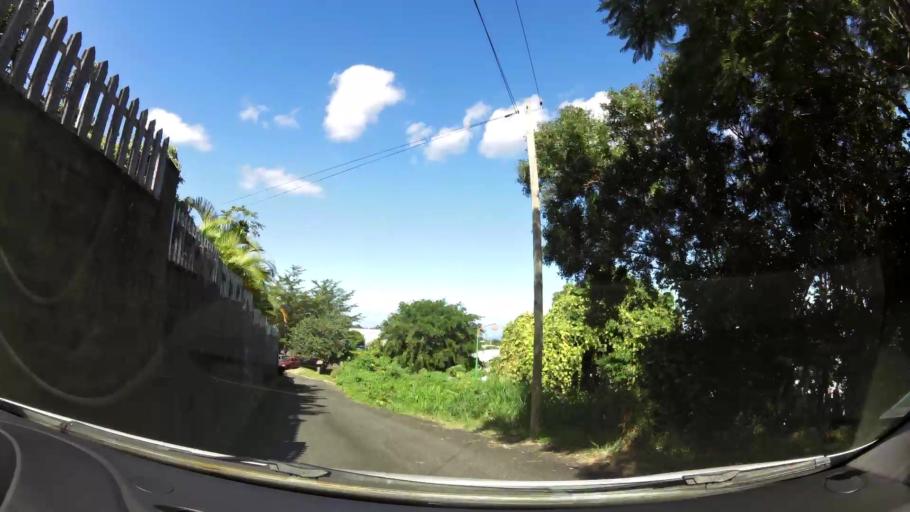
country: RE
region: Reunion
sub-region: Reunion
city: Le Tampon
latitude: -21.2784
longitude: 55.5037
